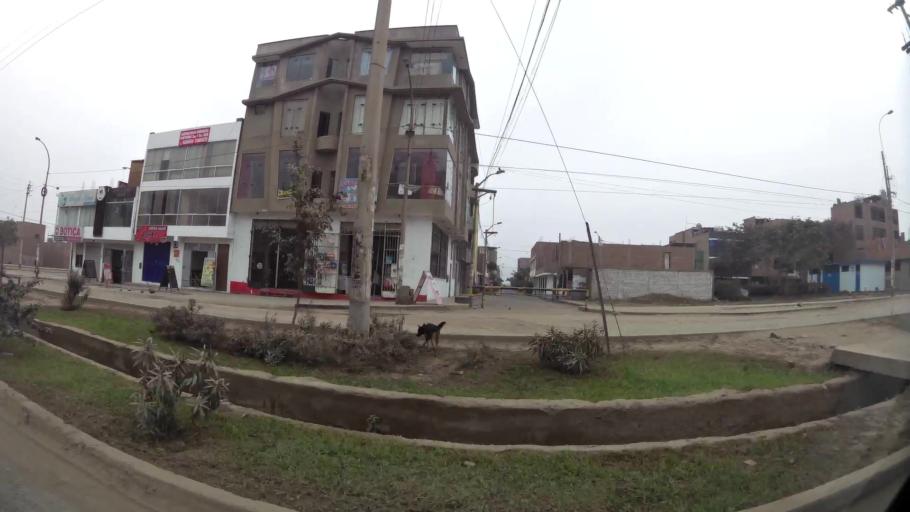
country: PE
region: Lima
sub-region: Lima
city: Urb. Santo Domingo
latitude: -11.8760
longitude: -77.0318
